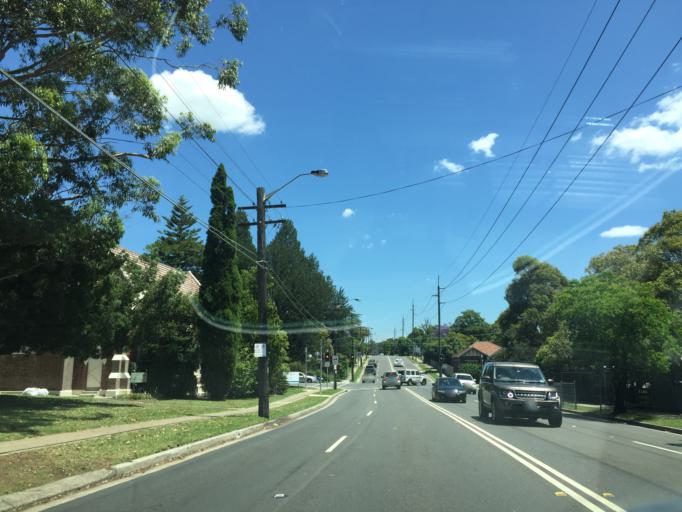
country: AU
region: New South Wales
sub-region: Ryde
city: Denistone
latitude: -33.7933
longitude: 151.0786
